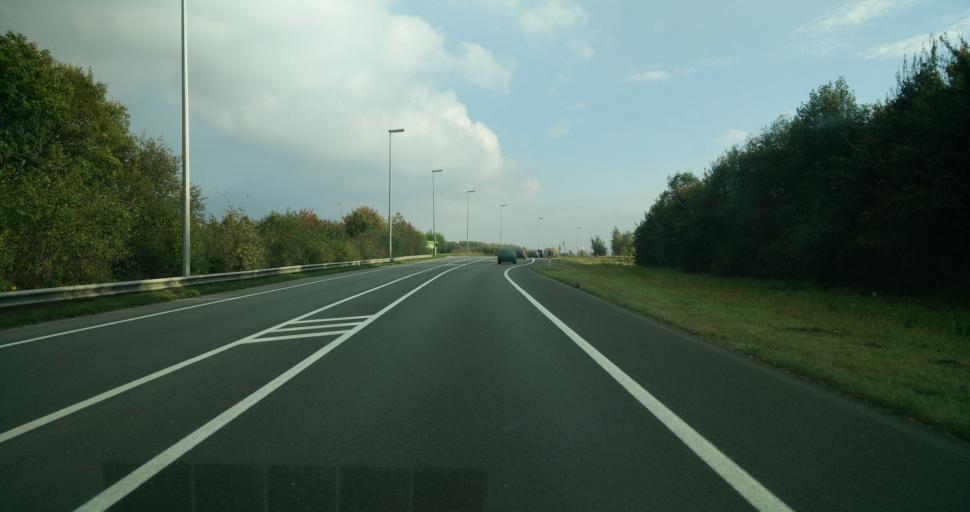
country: BE
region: Flanders
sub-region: Provincie Oost-Vlaanderen
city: Oosterzele
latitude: 50.9485
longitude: 3.8201
